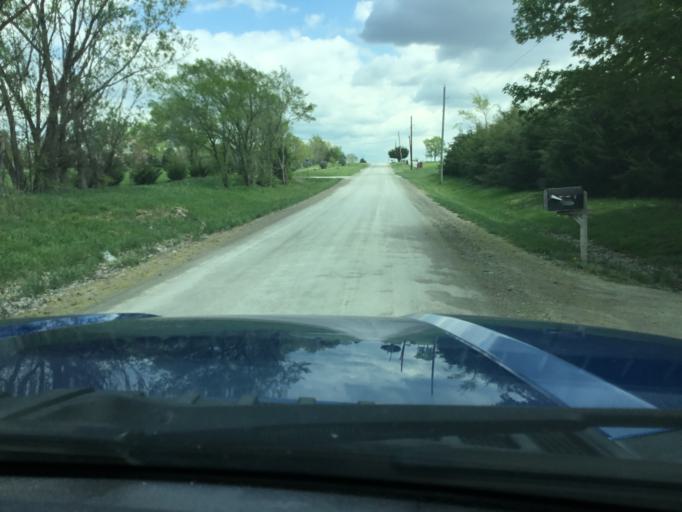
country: US
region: Kansas
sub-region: Douglas County
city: Eudora
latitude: 38.9132
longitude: -95.1105
